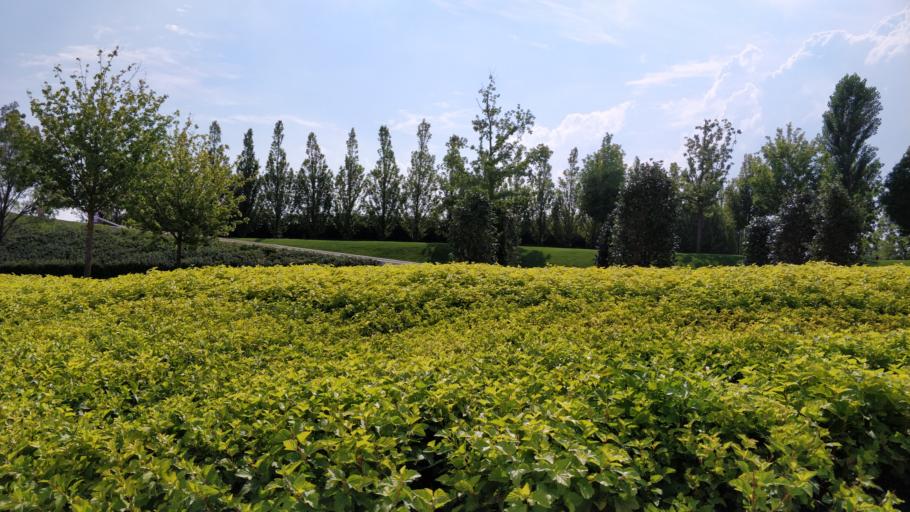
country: RU
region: Krasnodarskiy
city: Krasnodar
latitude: 45.0412
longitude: 39.0305
